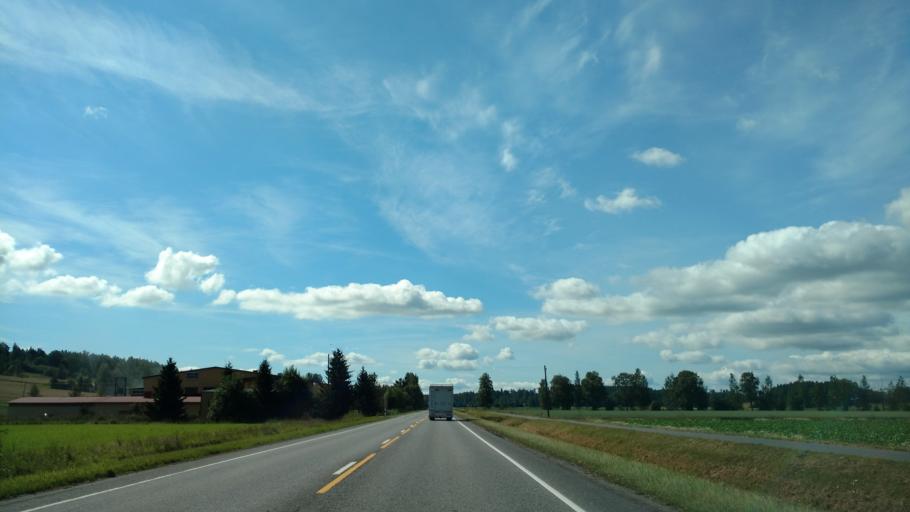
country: FI
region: Varsinais-Suomi
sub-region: Salo
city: Pernioe
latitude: 60.2339
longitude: 23.1243
